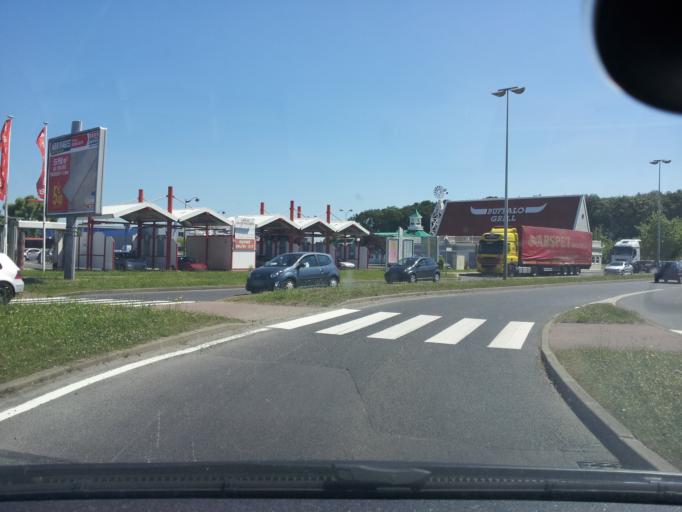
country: FR
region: Ile-de-France
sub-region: Departement de l'Essonne
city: Bretigny-sur-Orge
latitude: 48.5878
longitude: 2.3046
